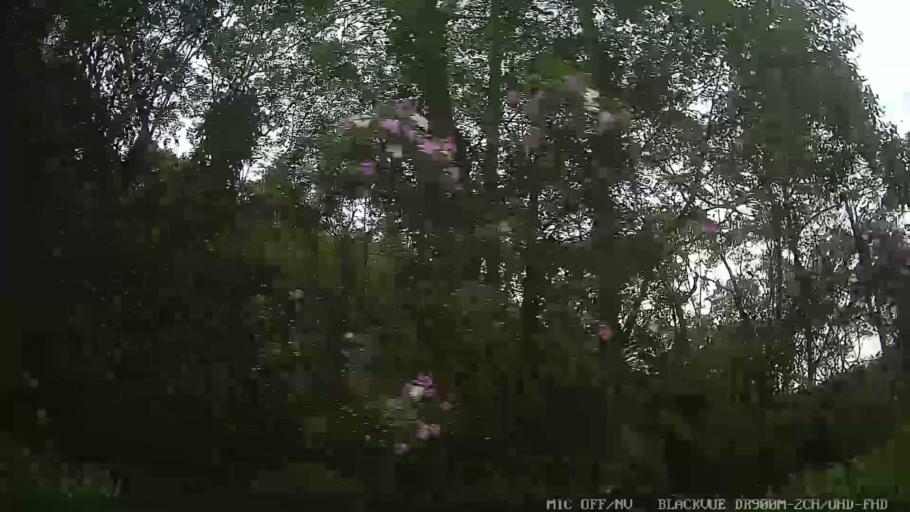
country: BR
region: Sao Paulo
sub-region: Ribeirao Pires
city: Ribeirao Pires
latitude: -23.7260
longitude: -46.4098
